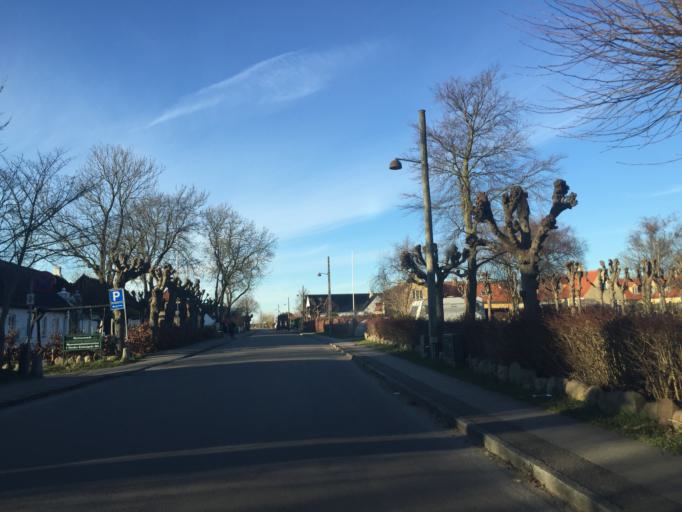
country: DK
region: Capital Region
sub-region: Dragor Kommune
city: Dragor
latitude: 55.5994
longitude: 12.6360
